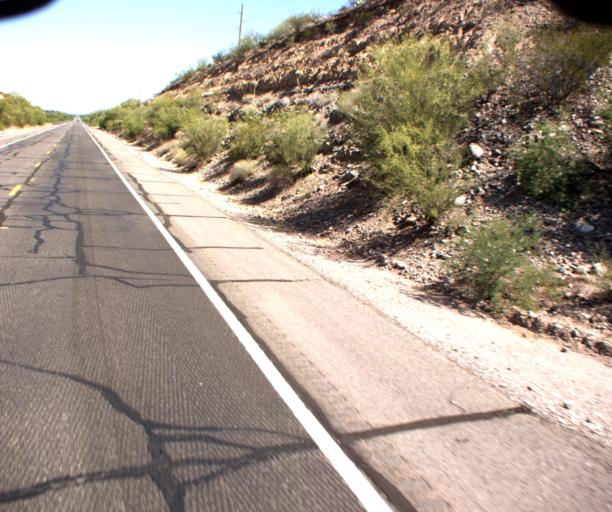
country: US
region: Arizona
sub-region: Pinal County
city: Mammoth
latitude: 32.7625
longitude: -110.6534
